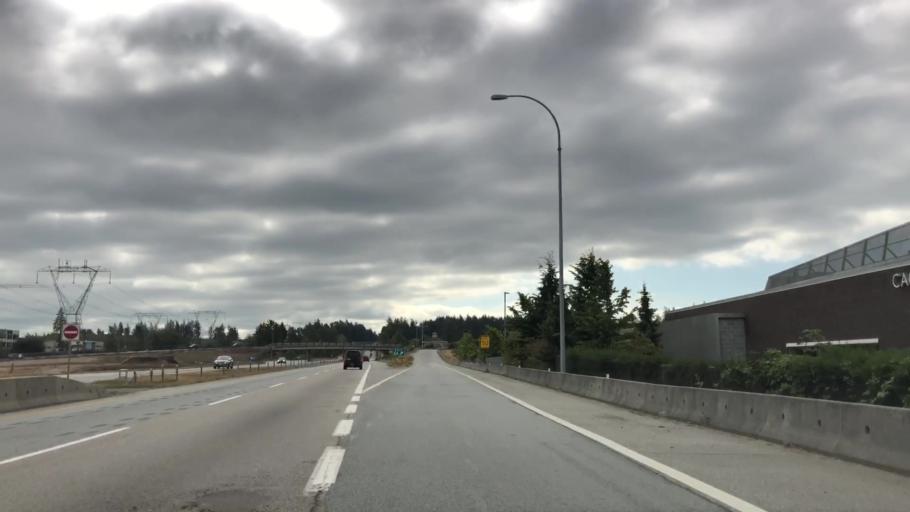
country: CA
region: British Columbia
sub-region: Greater Vancouver Regional District
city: White Rock
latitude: 49.0607
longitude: -122.8046
